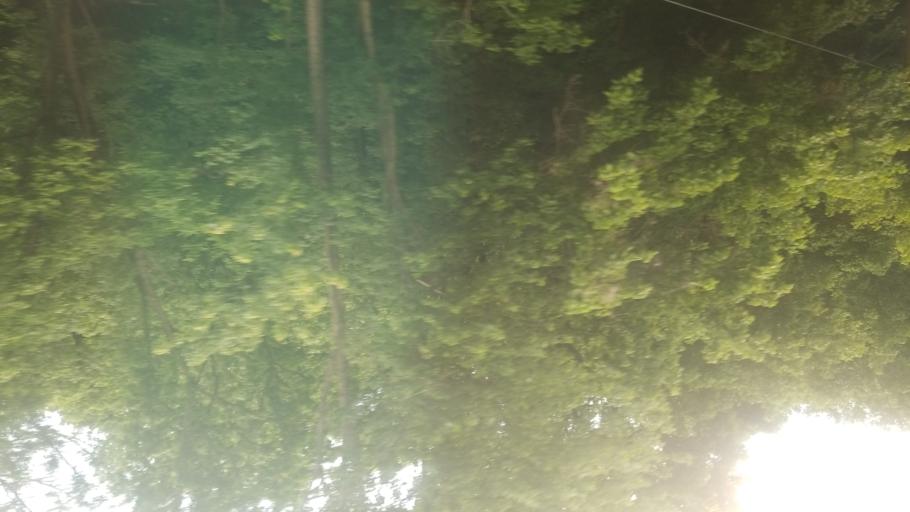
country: US
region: Maryland
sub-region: Frederick County
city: Brunswick
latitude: 39.3236
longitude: -77.6620
